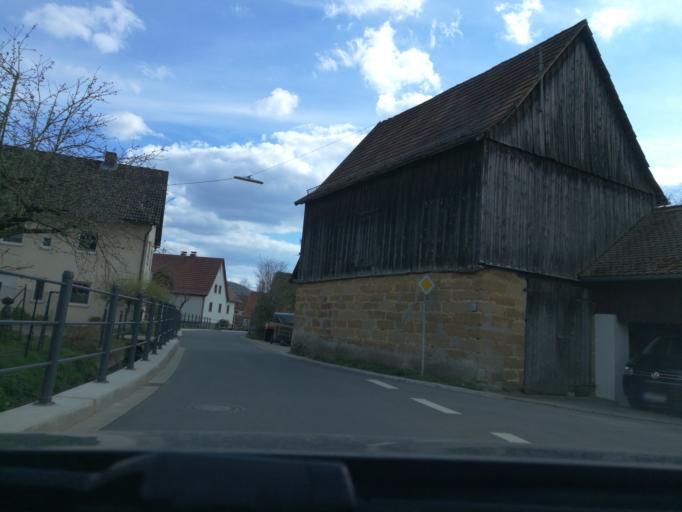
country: DE
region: Bavaria
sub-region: Upper Franconia
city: Weilersbach
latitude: 49.8202
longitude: 11.1158
